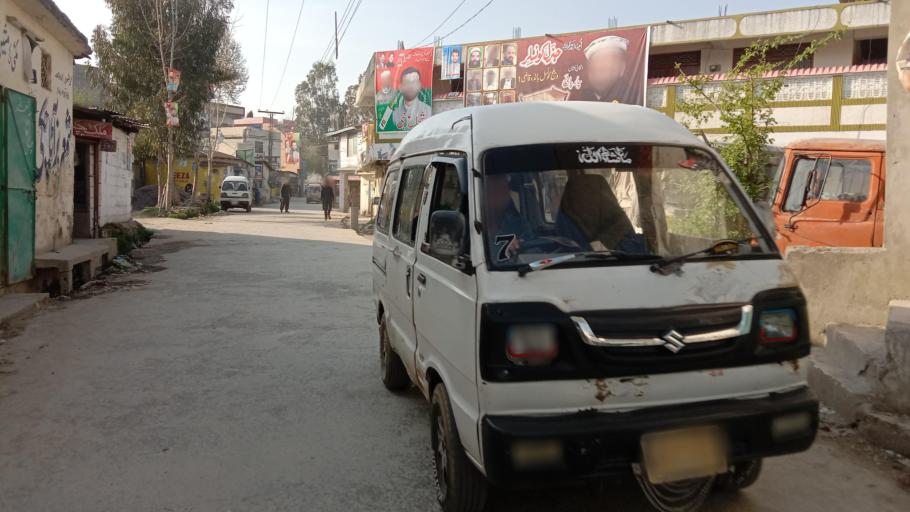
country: PK
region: Khyber Pakhtunkhwa
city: Abbottabad
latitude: 34.2010
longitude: 73.2265
